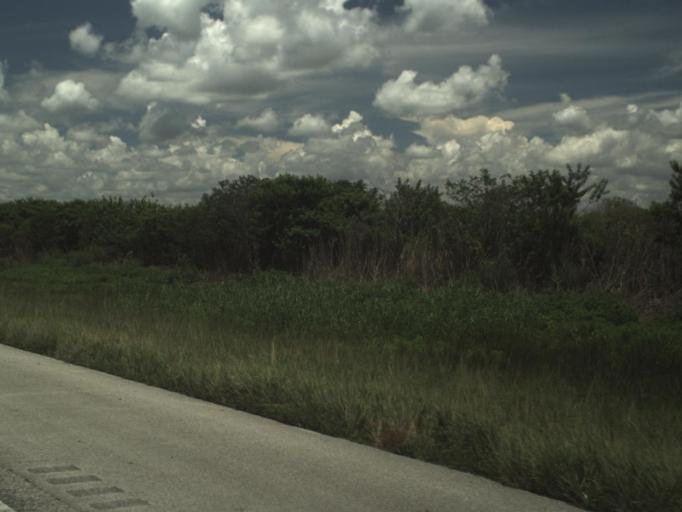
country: US
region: Florida
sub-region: Broward County
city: Weston
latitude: 26.1612
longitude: -80.7937
